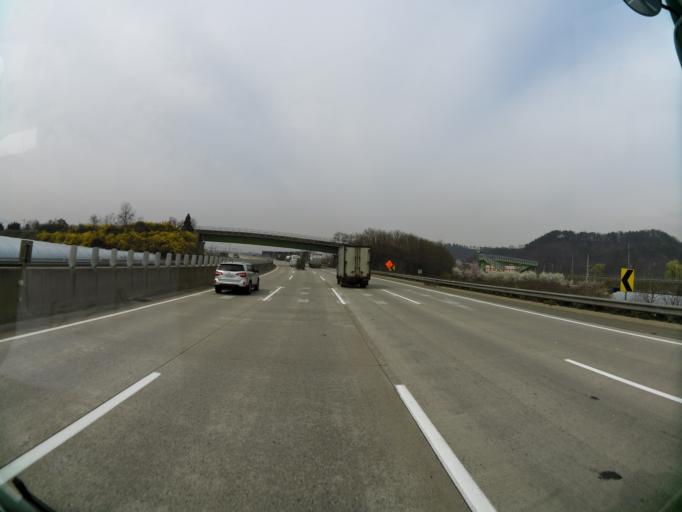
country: KR
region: Gyeongsangbuk-do
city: Hayang
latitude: 35.8798
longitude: 128.7705
